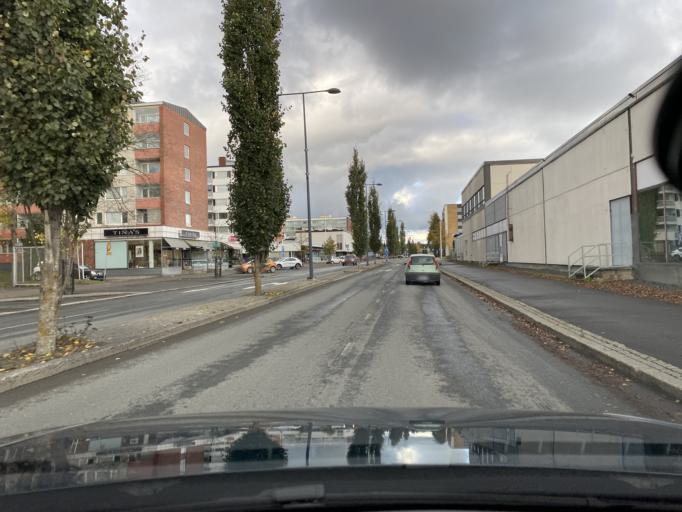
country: FI
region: Haeme
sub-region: Forssa
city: Forssa
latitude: 60.8167
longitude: 23.6275
